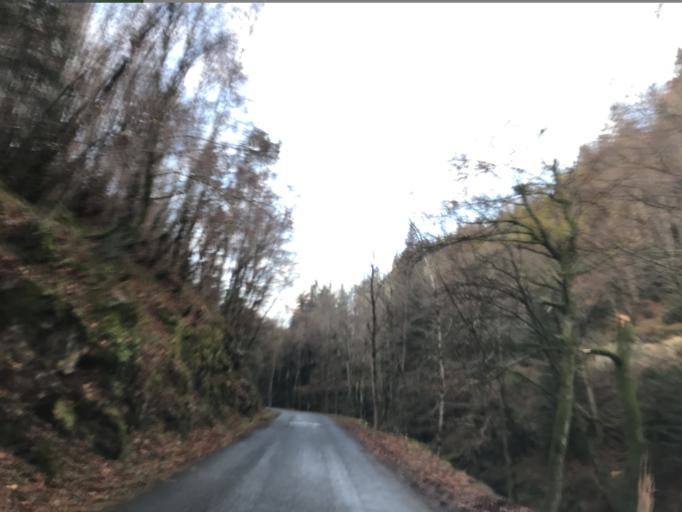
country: FR
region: Auvergne
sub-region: Departement du Puy-de-Dome
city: Courpiere
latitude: 45.7607
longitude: 3.6322
